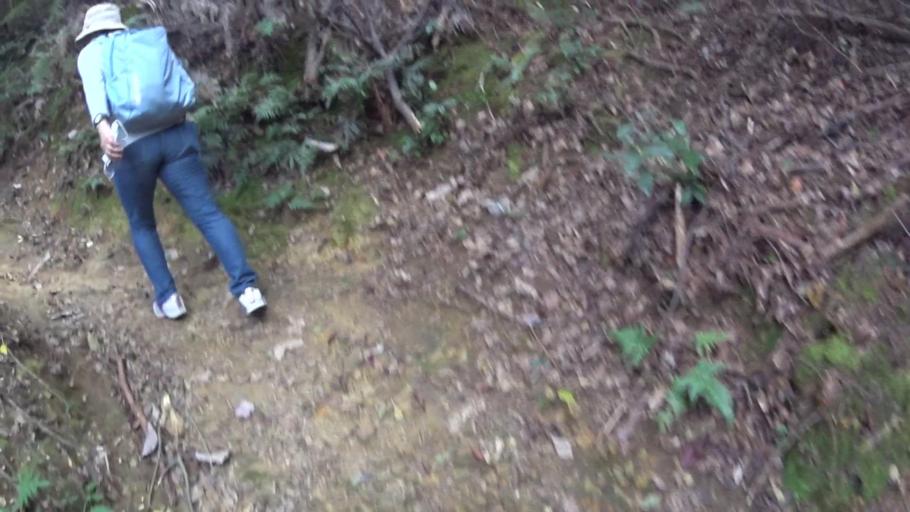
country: JP
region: Osaka
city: Kaizuka
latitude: 34.4758
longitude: 135.3084
